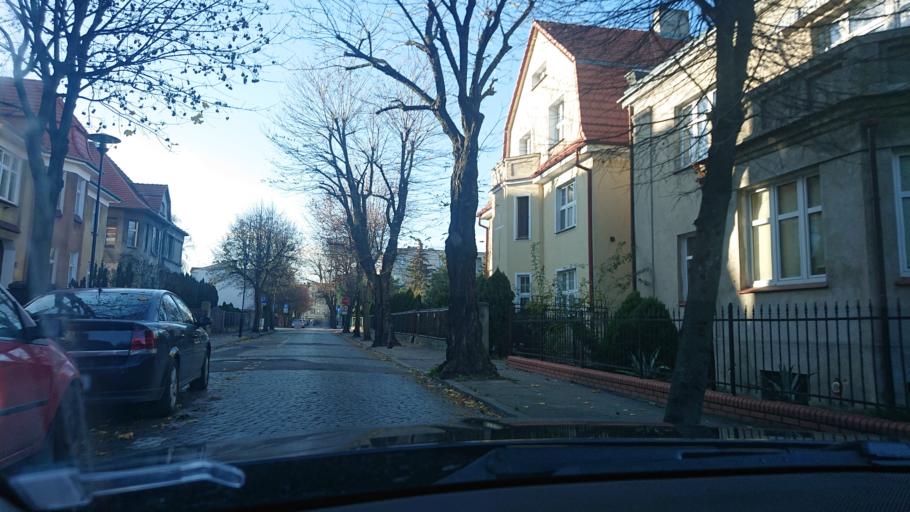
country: PL
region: Greater Poland Voivodeship
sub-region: Powiat gnieznienski
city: Gniezno
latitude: 52.5385
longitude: 17.6049
